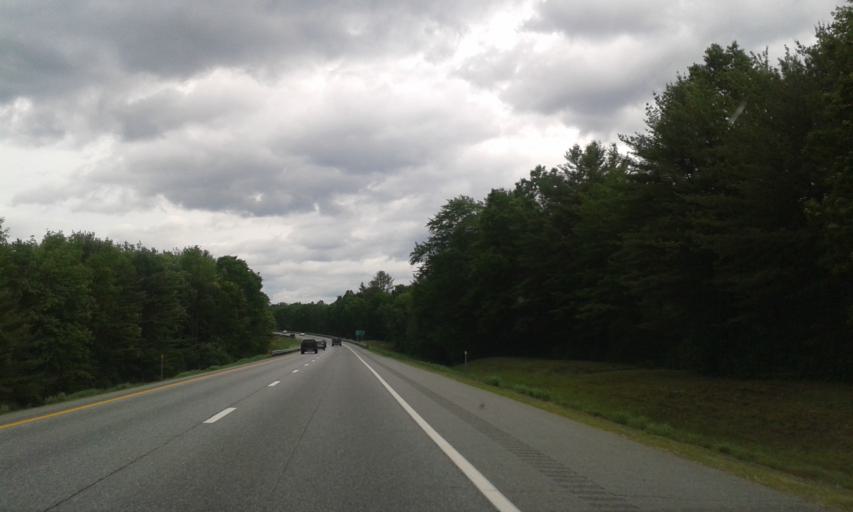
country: US
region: New Hampshire
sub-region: Merrimack County
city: East Concord
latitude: 43.2780
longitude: -71.5654
